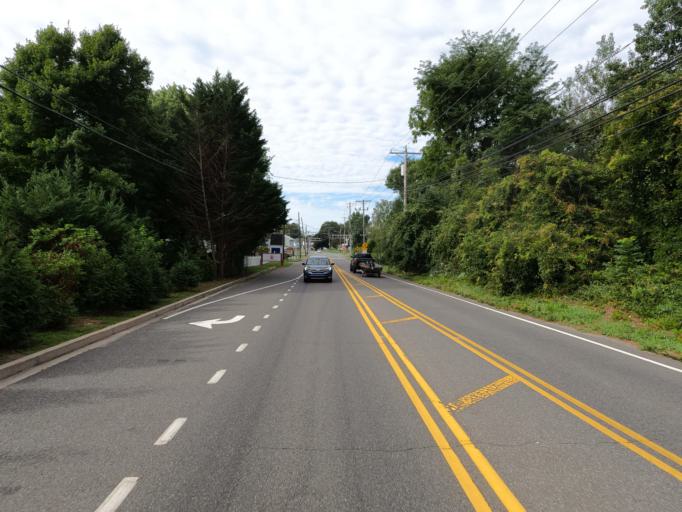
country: US
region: Delaware
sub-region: New Castle County
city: Glasgow
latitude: 39.5729
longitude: -75.6954
